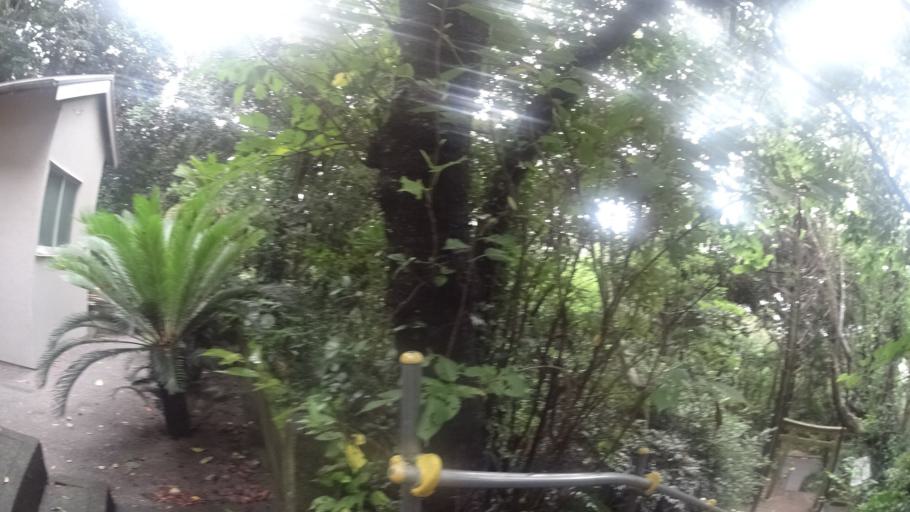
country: JP
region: Shizuoka
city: Shimoda
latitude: 34.3231
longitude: 139.2199
